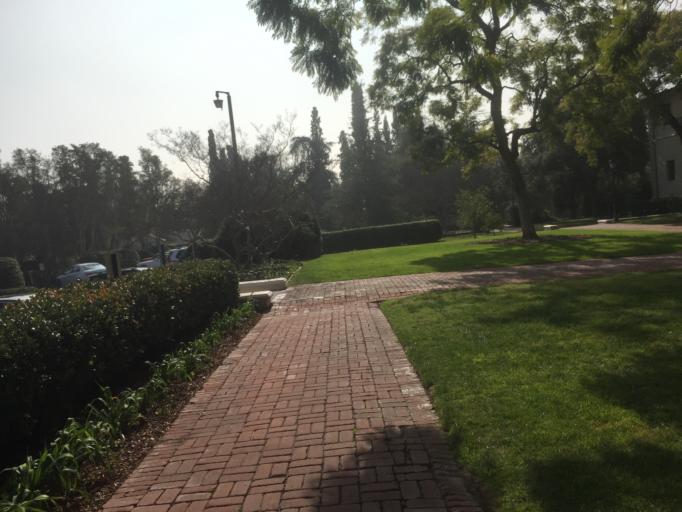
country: US
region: California
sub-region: Los Angeles County
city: San Marino
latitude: 34.1366
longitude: -118.1221
